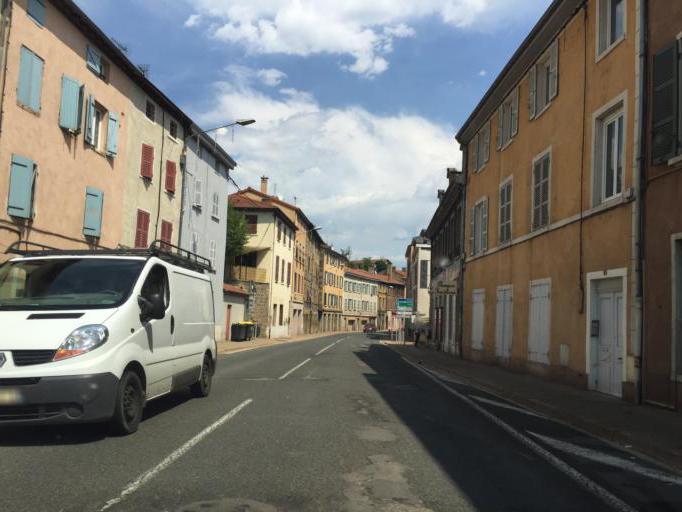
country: FR
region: Rhone-Alpes
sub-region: Departement du Rhone
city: Saint-Germain-Nuelles
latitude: 45.8374
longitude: 4.6147
